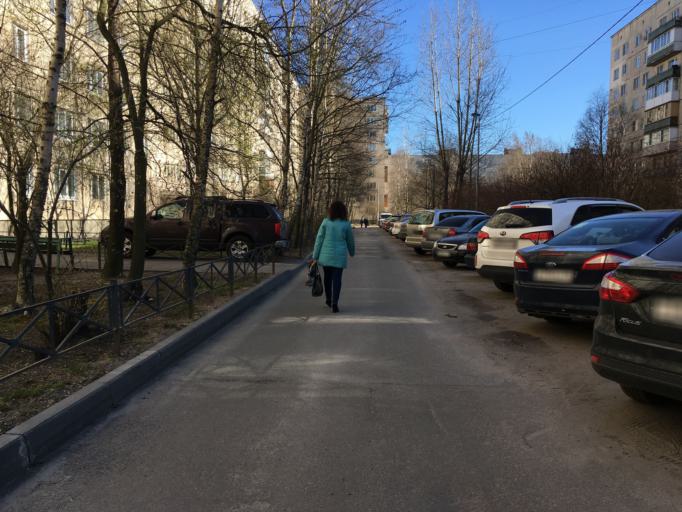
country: RU
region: St.-Petersburg
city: Obukhovo
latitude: 59.9062
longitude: 30.4651
